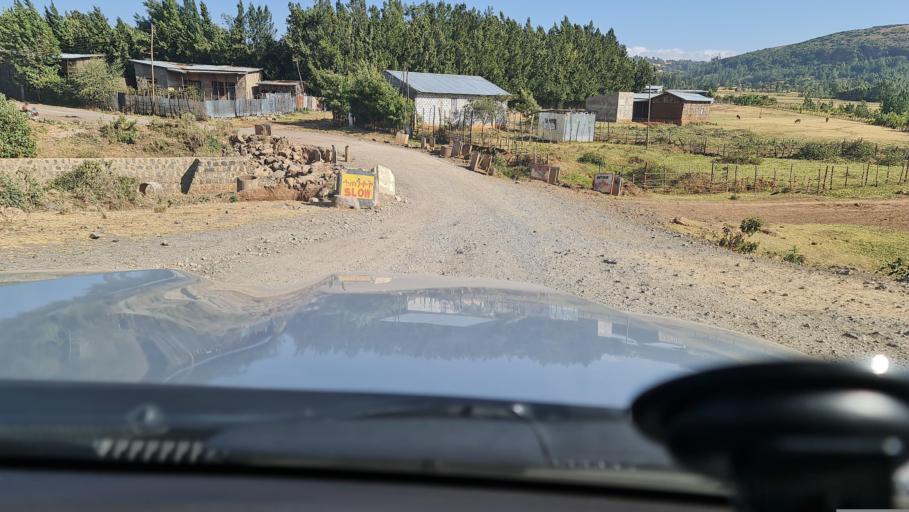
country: ET
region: Oromiya
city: Waliso
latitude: 8.6041
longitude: 37.9273
